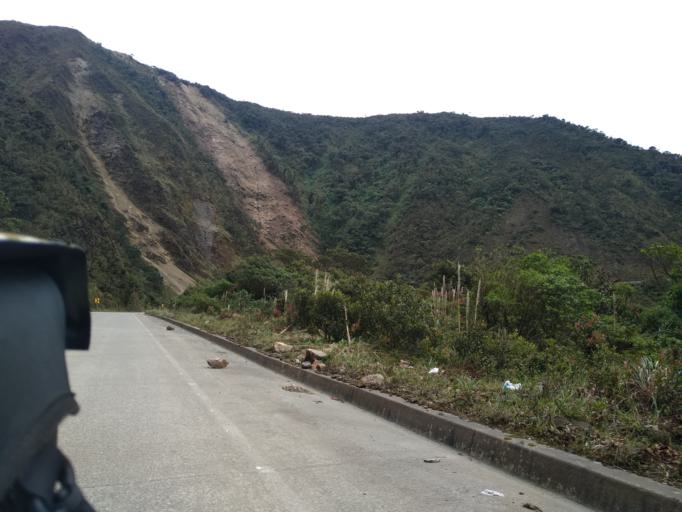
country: EC
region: Zamora-Chinchipe
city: Zamora
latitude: -4.4357
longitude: -79.1475
